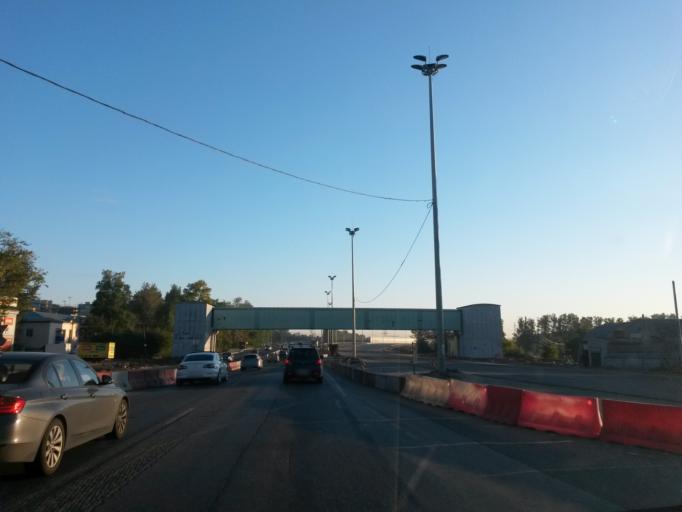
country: RU
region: Moskovskaya
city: Bolshevo
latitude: 55.9431
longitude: 37.8133
